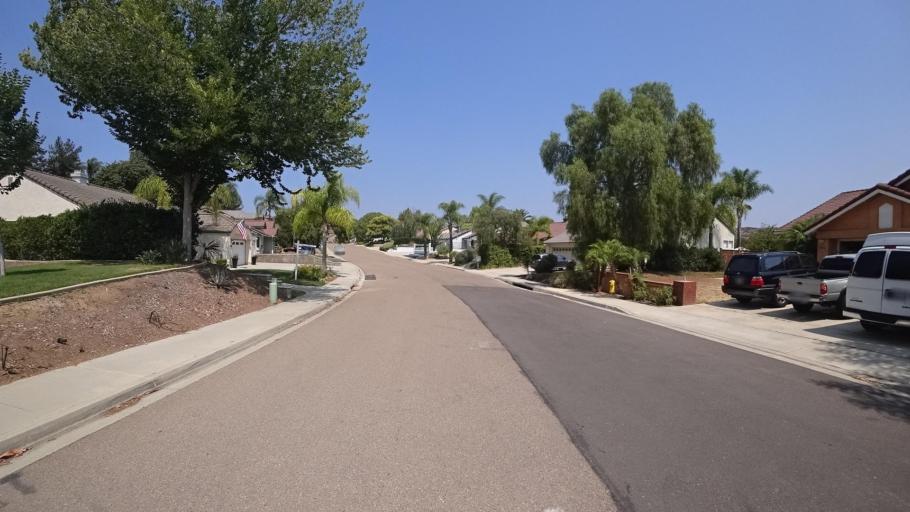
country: US
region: California
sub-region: San Diego County
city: Bonsall
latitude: 33.2945
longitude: -117.2257
